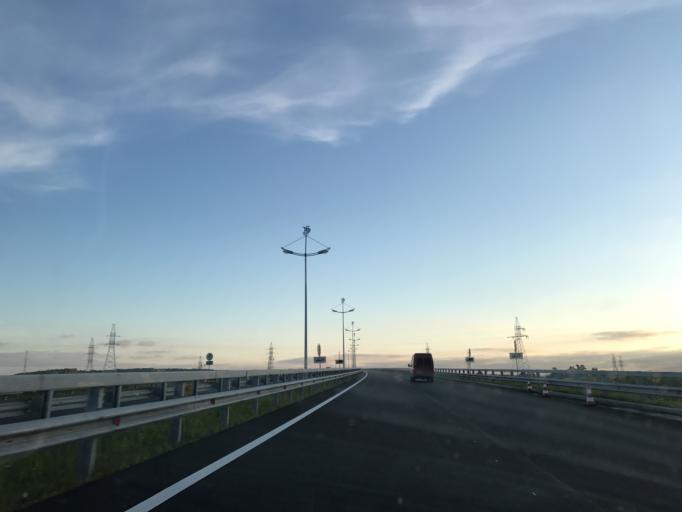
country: RU
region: Kaliningrad
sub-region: Gorod Kaliningrad
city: Pionerskiy
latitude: 54.9175
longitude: 20.2406
